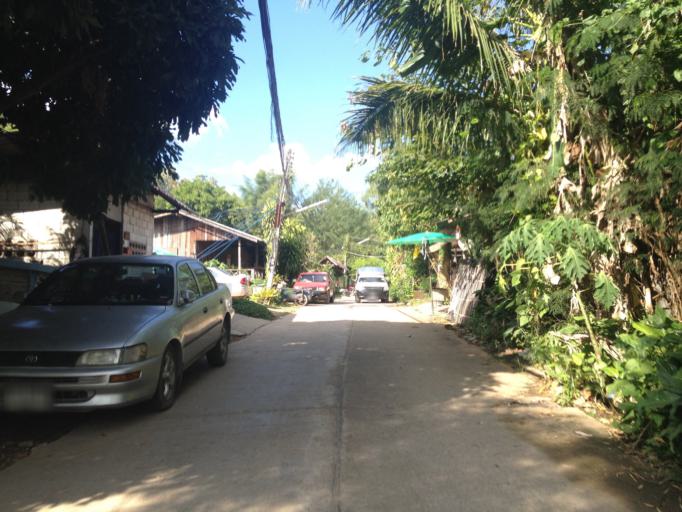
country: TH
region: Chiang Mai
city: Chiang Mai
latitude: 18.7783
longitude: 98.9477
